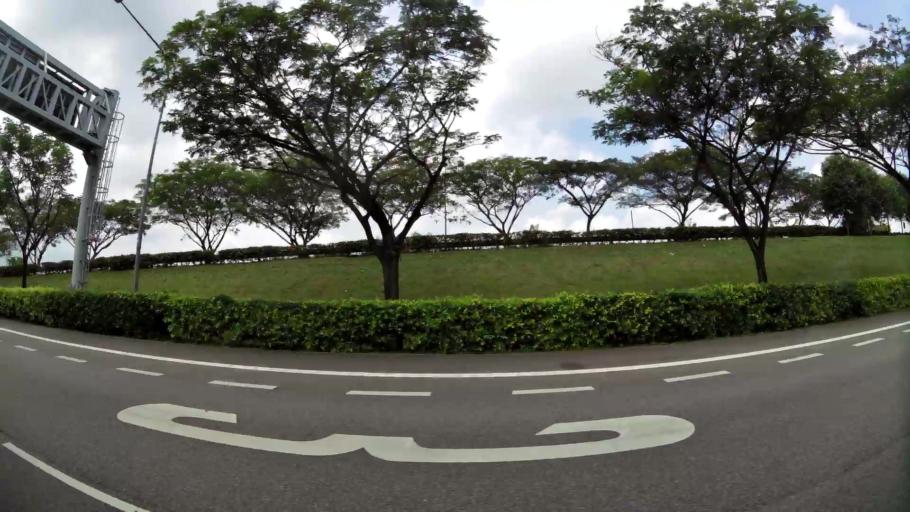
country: MY
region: Johor
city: Kampung Pasir Gudang Baru
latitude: 1.3755
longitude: 103.9096
